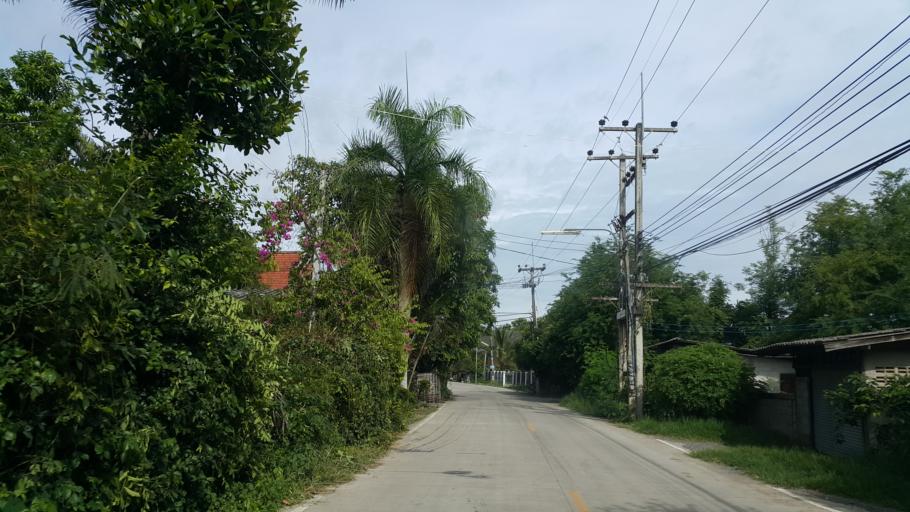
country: TH
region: Chiang Mai
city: San Kamphaeng
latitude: 18.7216
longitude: 99.0884
